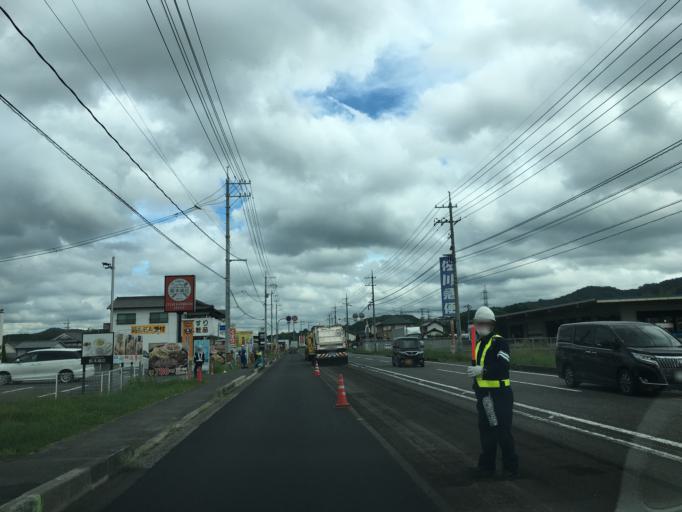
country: JP
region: Okayama
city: Okayama-shi
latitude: 34.7589
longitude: 134.0266
